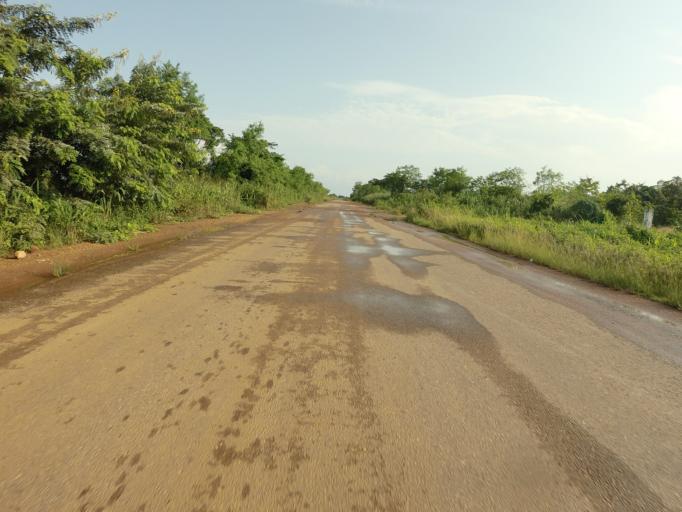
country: GH
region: Volta
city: Hohoe
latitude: 7.0684
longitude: 0.4346
